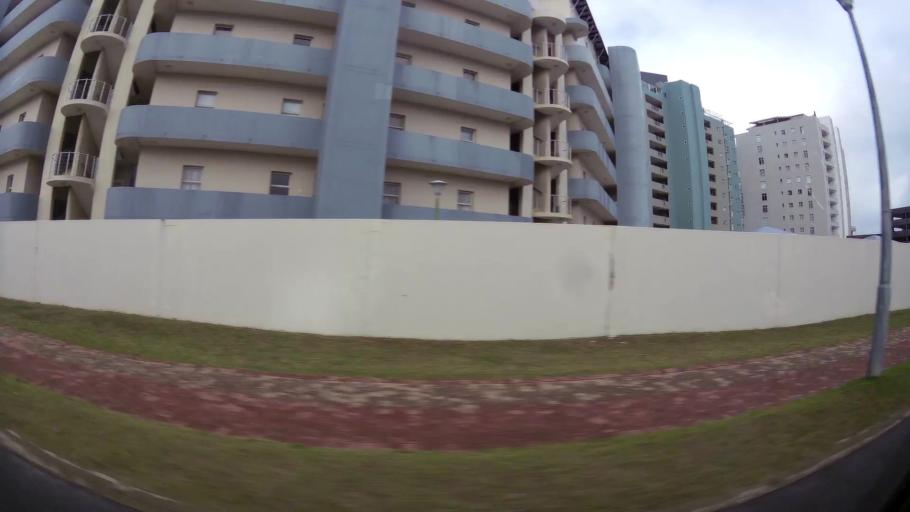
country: ZA
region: Western Cape
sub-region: Eden District Municipality
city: Mossel Bay
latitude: -34.1574
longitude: 22.1088
